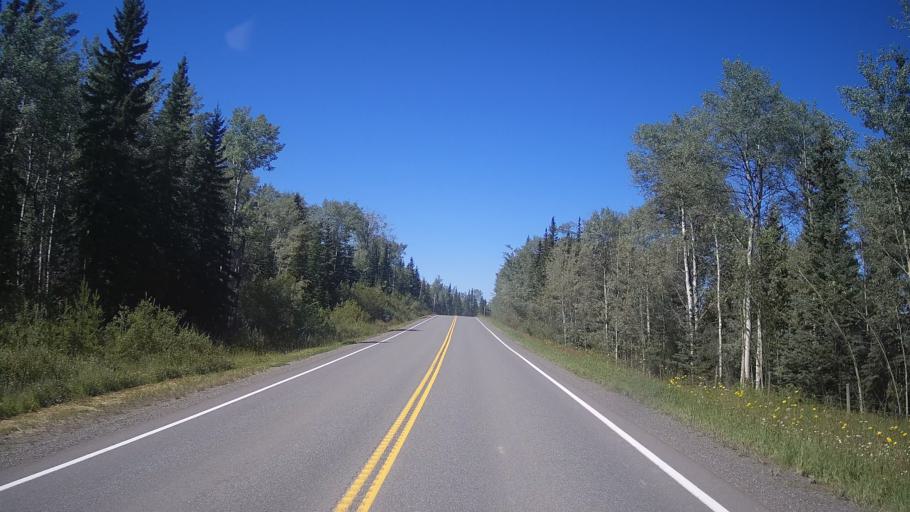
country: CA
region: British Columbia
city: Cache Creek
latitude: 51.5469
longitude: -120.9292
